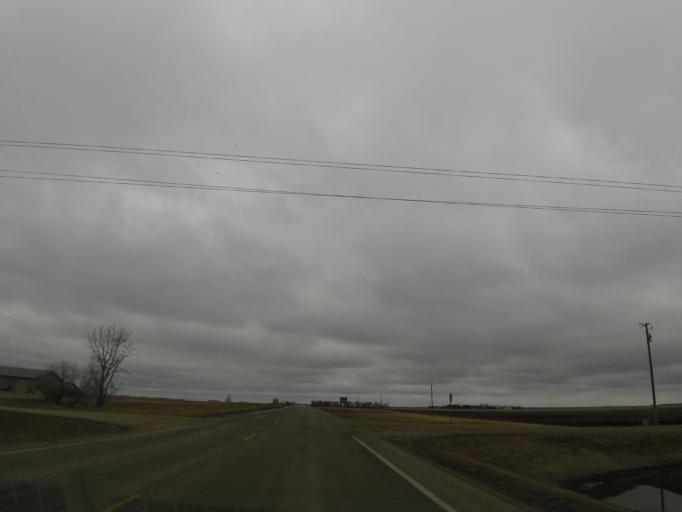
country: US
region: North Dakota
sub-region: Traill County
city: Hillsboro
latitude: 47.1949
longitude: -97.2175
